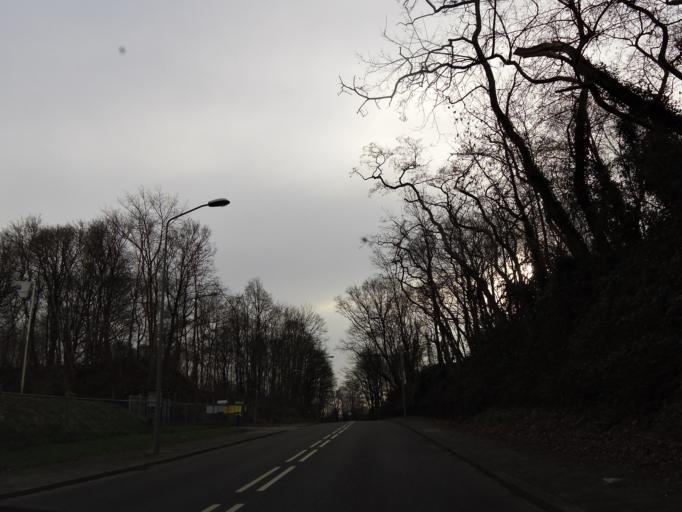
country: NL
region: Limburg
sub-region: Gemeente Nuth
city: Nuth
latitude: 50.9203
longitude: 5.9050
